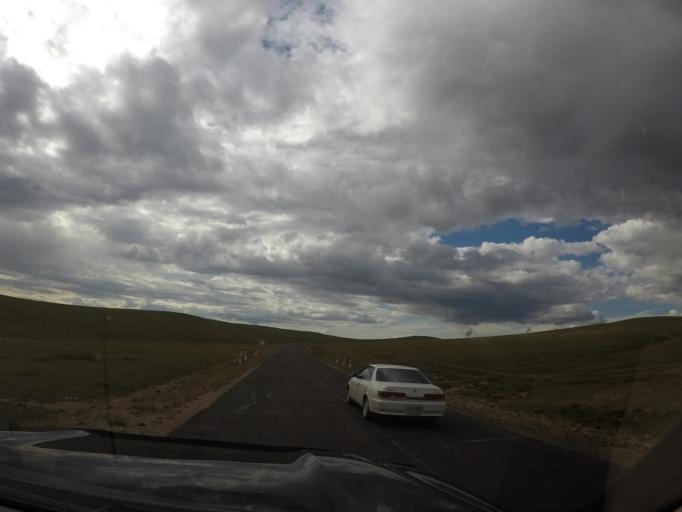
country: MN
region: Hentiy
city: Modot
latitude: 47.5661
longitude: 109.3141
